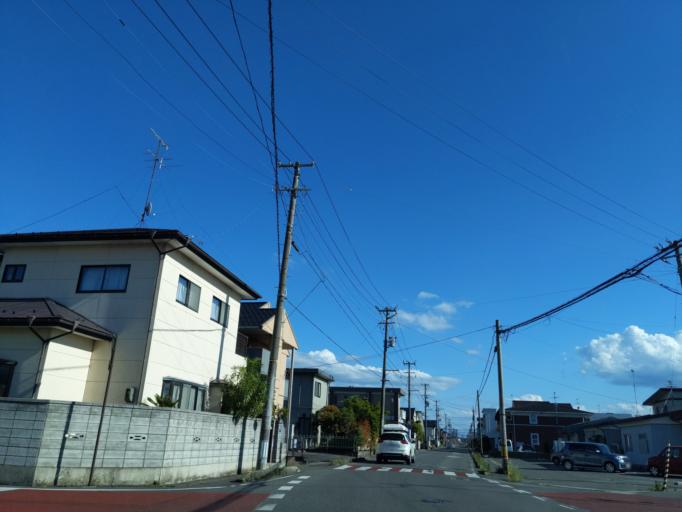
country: JP
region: Fukushima
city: Koriyama
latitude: 37.3907
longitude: 140.3356
